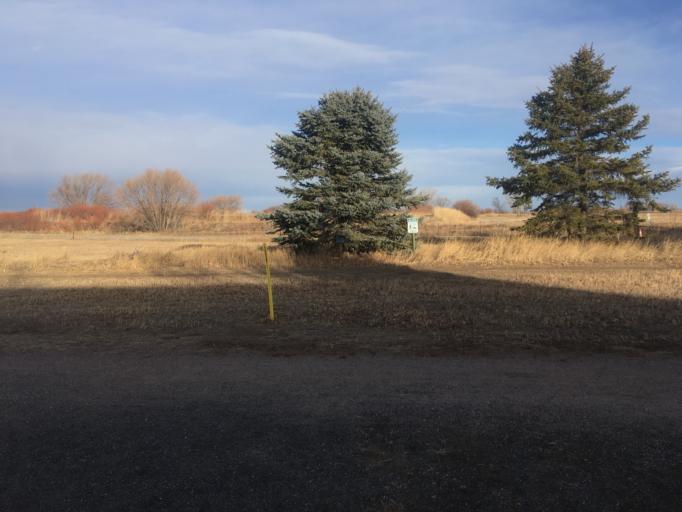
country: US
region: Colorado
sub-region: Boulder County
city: Lafayette
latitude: 40.0168
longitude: -105.0841
